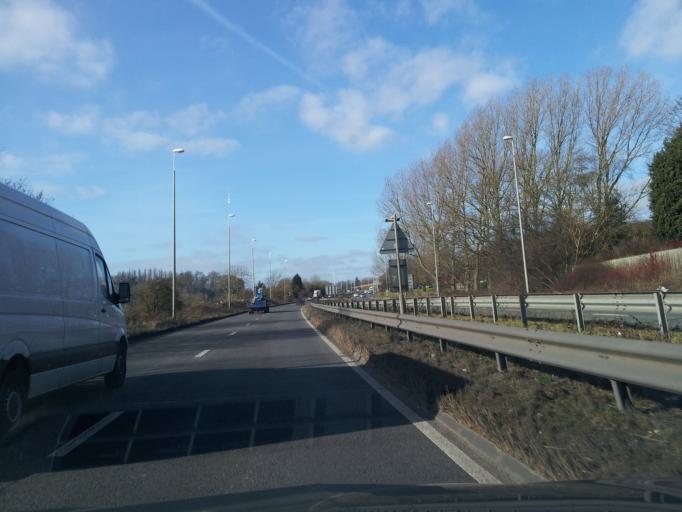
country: GB
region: England
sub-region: Nottinghamshire
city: Ruddington
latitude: 52.9021
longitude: -1.1247
